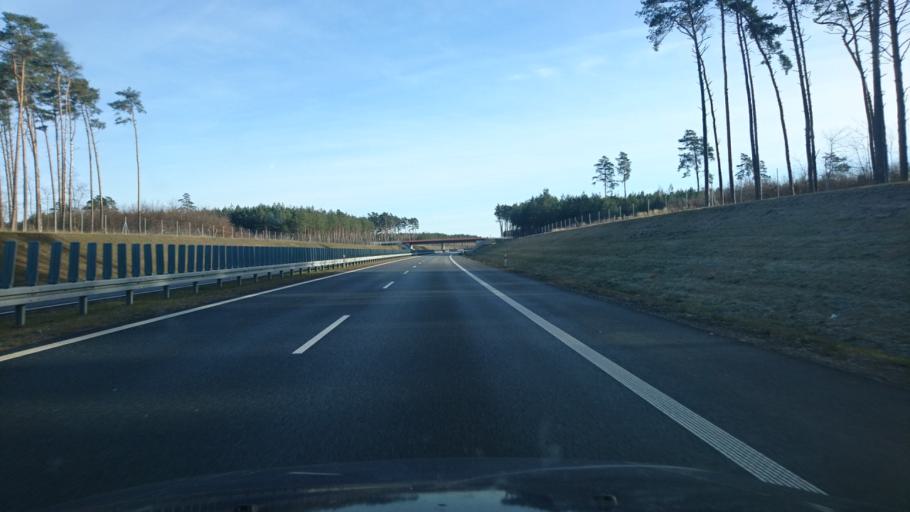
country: PL
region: Greater Poland Voivodeship
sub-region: Powiat kepinski
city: Kepno
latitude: 51.3305
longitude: 17.9699
